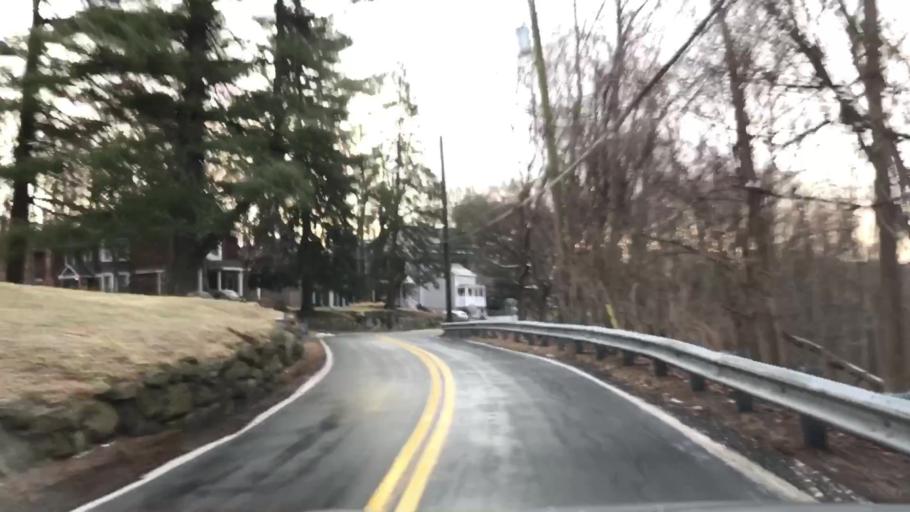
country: US
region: New York
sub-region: Rockland County
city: Stony Point
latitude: 41.2357
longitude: -74.0035
